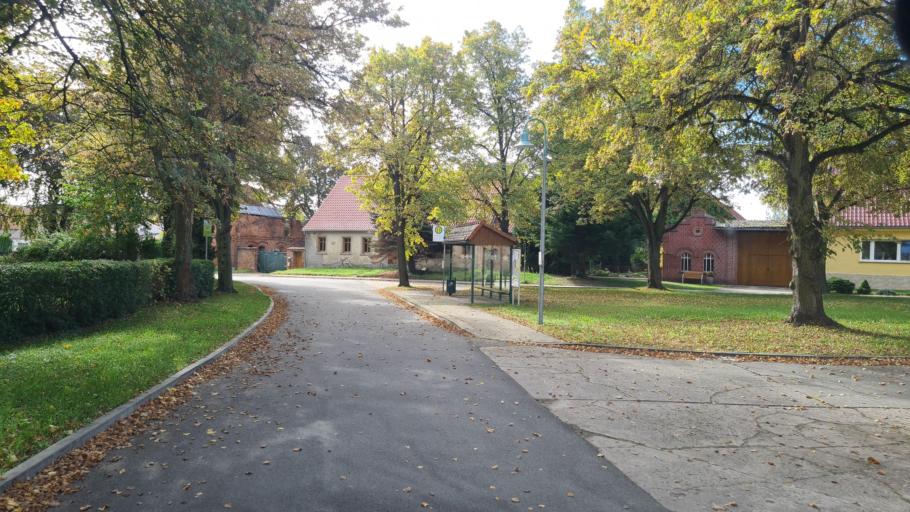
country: DE
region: Brandenburg
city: Linthe
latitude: 52.1108
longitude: 12.7482
